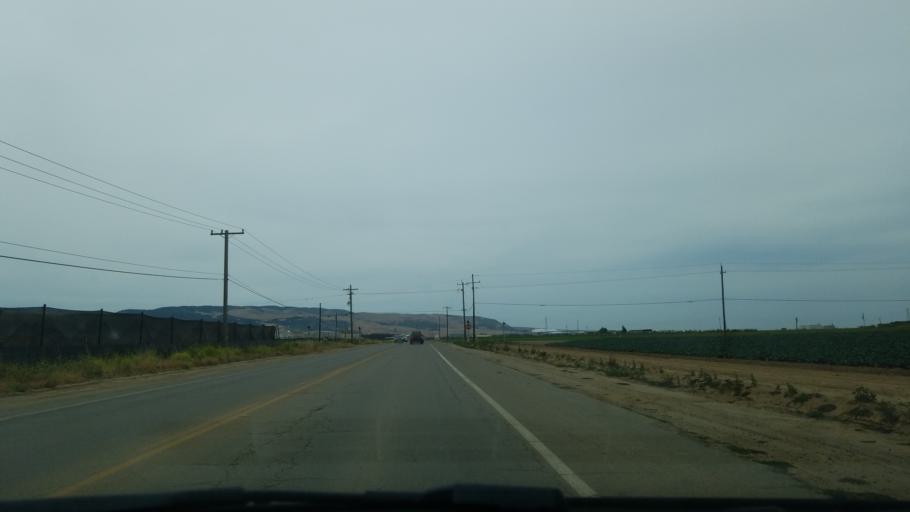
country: US
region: California
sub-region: Santa Barbara County
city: Santa Maria
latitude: 34.9209
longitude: -120.4887
